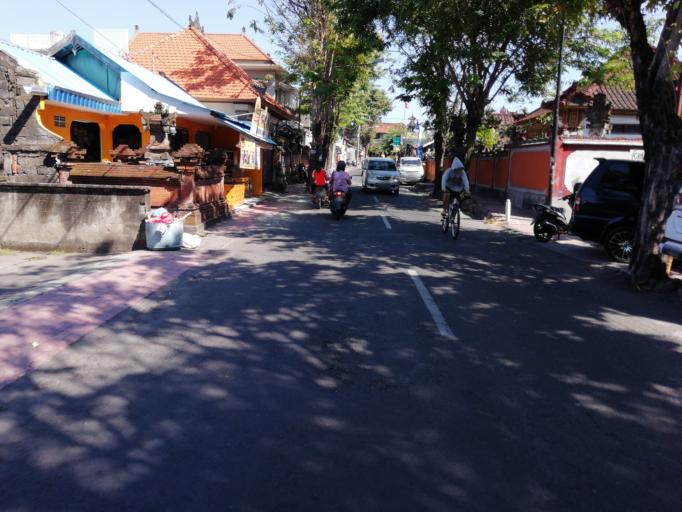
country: ID
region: Bali
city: Karyadharma
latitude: -8.6996
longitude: 115.2274
